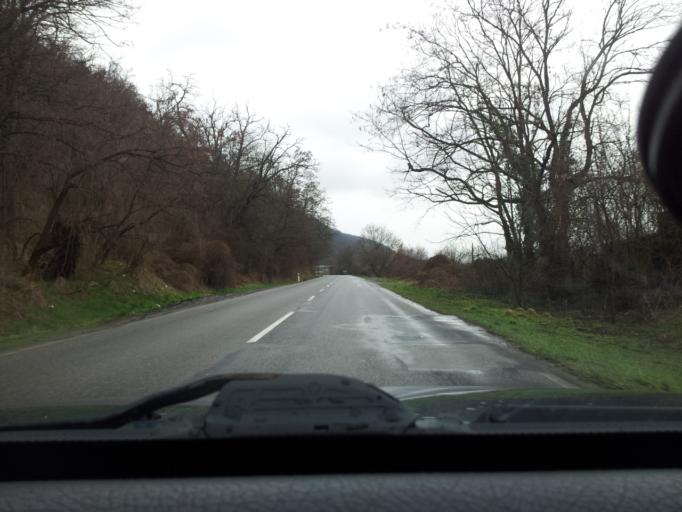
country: SK
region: Nitriansky
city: Tlmace
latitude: 48.3553
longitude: 18.5706
